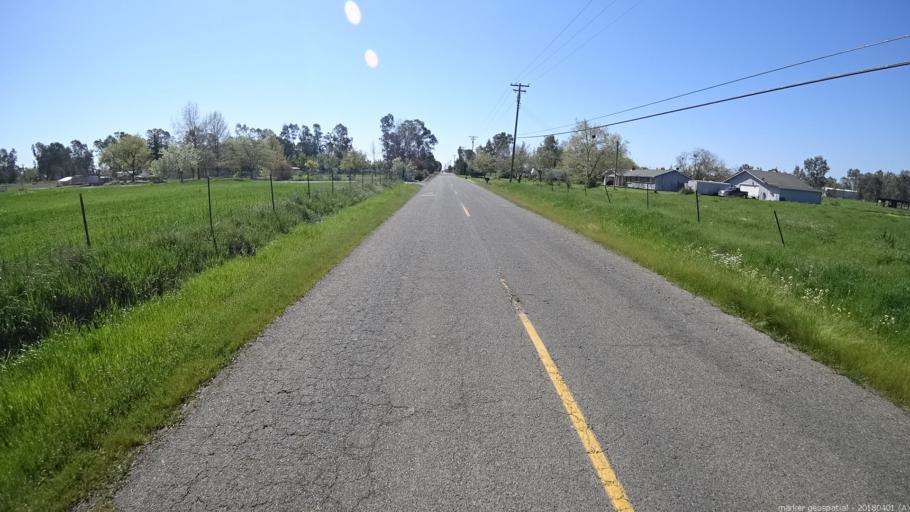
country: US
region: California
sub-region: Sacramento County
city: Wilton
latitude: 38.3837
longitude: -121.2422
